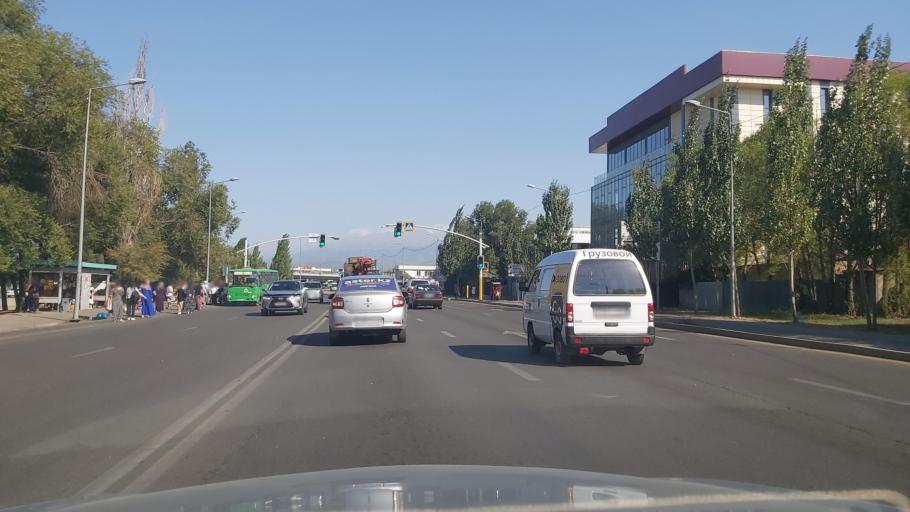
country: KZ
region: Almaty Qalasy
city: Almaty
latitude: 43.3026
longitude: 76.8919
